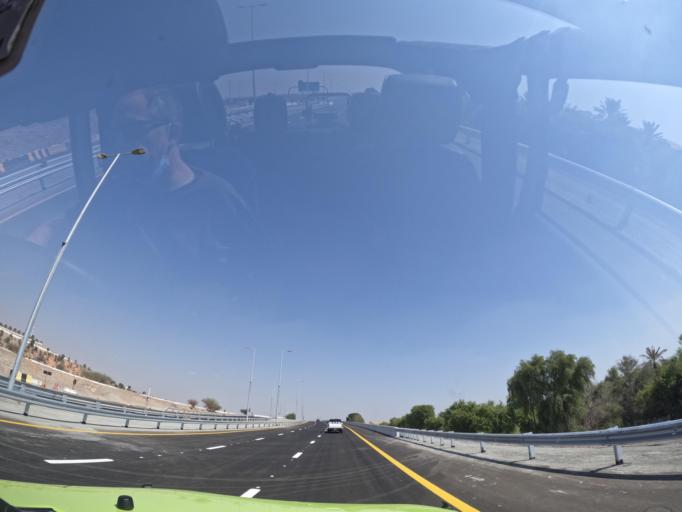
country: AE
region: Ash Shariqah
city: Adh Dhayd
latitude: 24.7781
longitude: 55.8140
